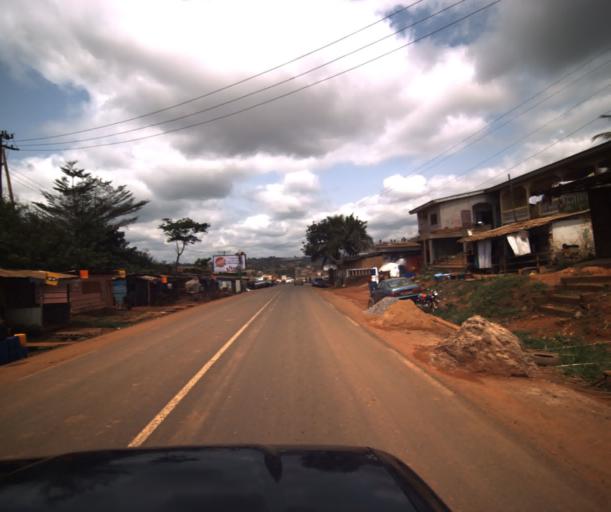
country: CM
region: Centre
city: Yaounde
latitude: 3.7953
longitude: 11.4950
